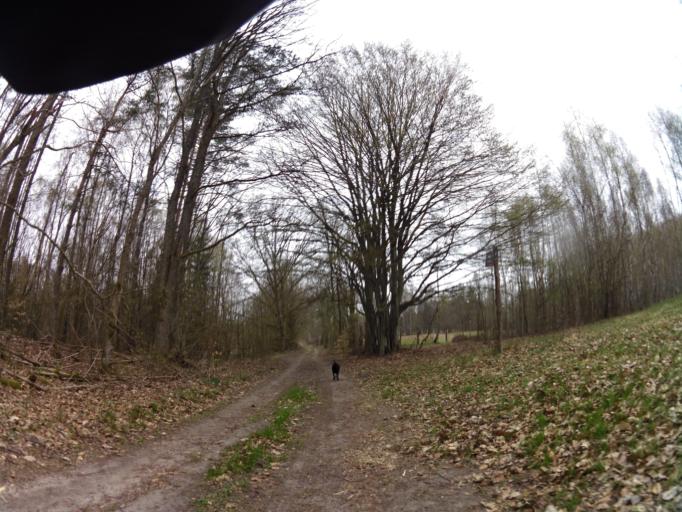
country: PL
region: West Pomeranian Voivodeship
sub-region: Powiat koszalinski
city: Bobolice
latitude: 53.9384
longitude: 16.6987
